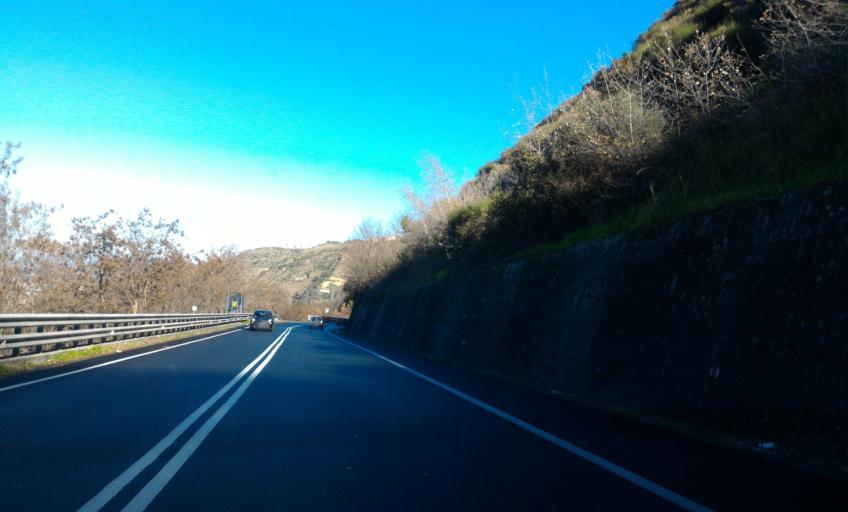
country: IT
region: Calabria
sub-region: Provincia di Cosenza
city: Cosenza
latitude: 39.2959
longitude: 16.2644
